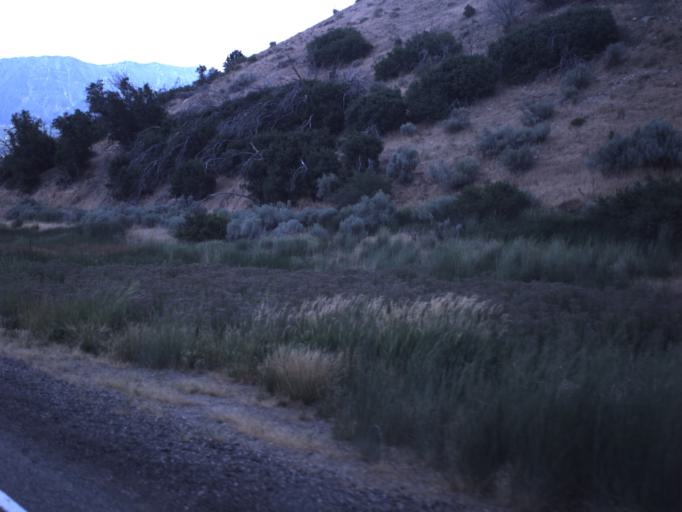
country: US
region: Utah
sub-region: Sanpete County
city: Fountain Green
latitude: 39.7059
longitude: -111.7107
